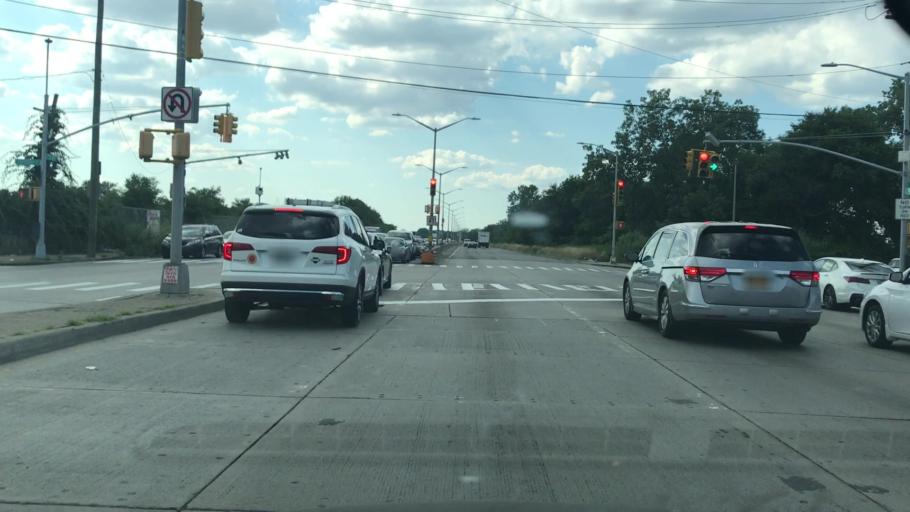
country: US
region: New York
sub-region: Nassau County
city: Inwood
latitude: 40.6405
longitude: -73.7431
